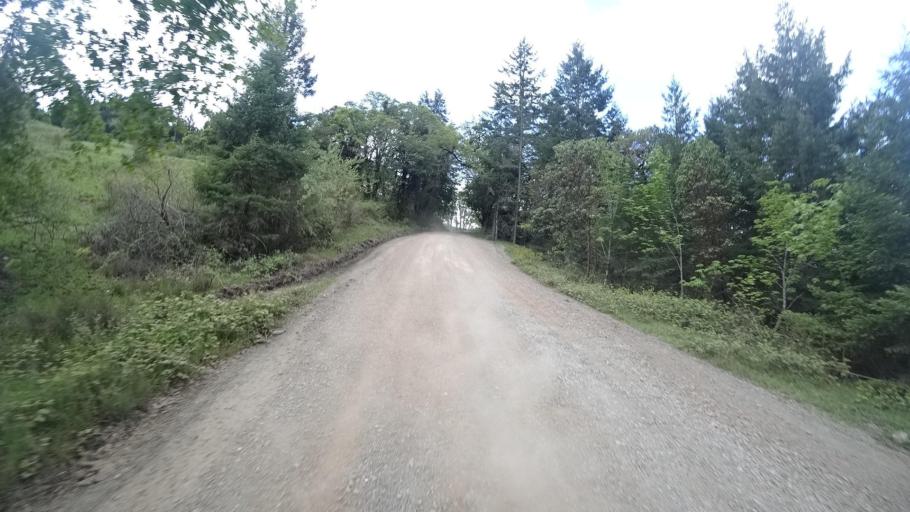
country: US
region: California
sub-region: Humboldt County
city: Redway
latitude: 40.1752
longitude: -123.5698
